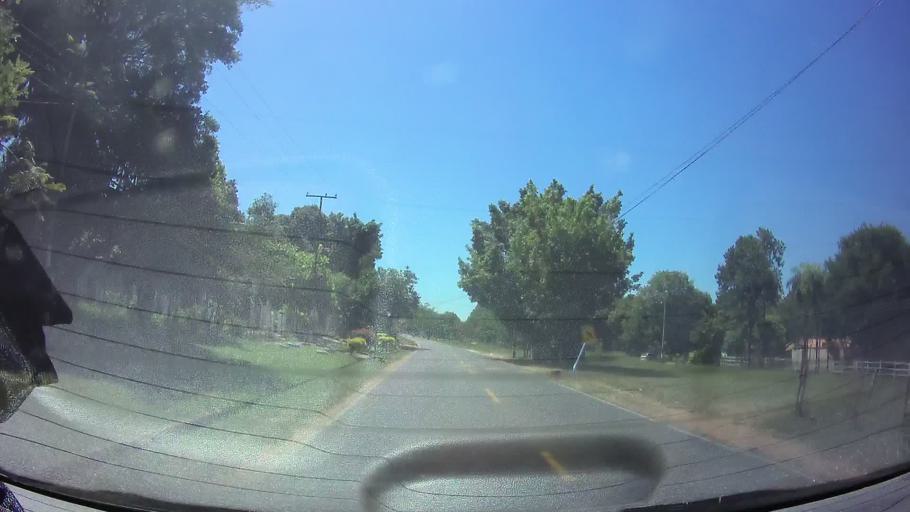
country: PY
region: Central
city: Aregua
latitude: -25.2808
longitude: -57.4001
